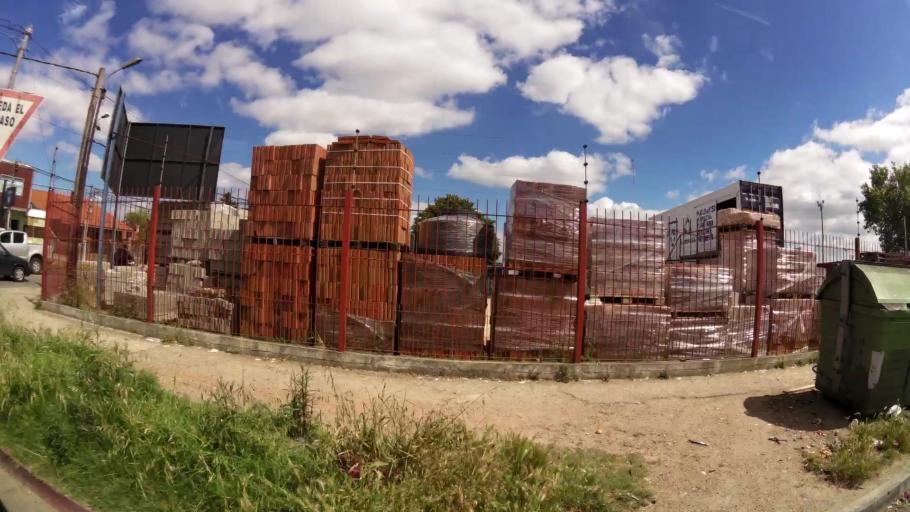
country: UY
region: Canelones
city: Paso de Carrasco
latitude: -34.8651
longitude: -56.1213
